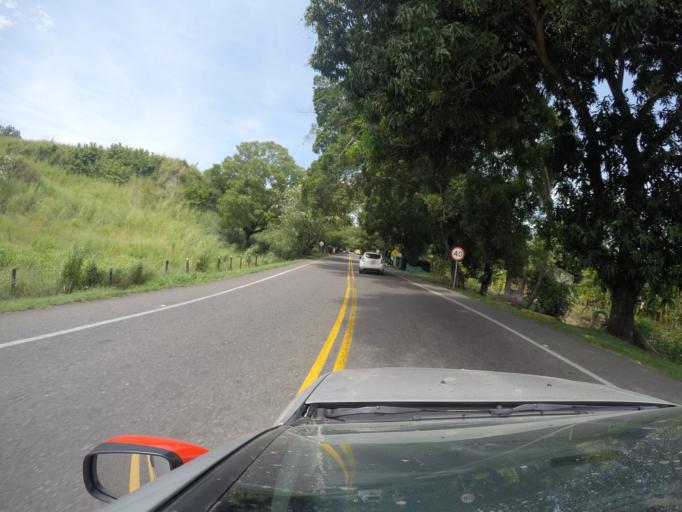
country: CO
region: Tolima
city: Honda
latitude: 5.3109
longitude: -74.7375
